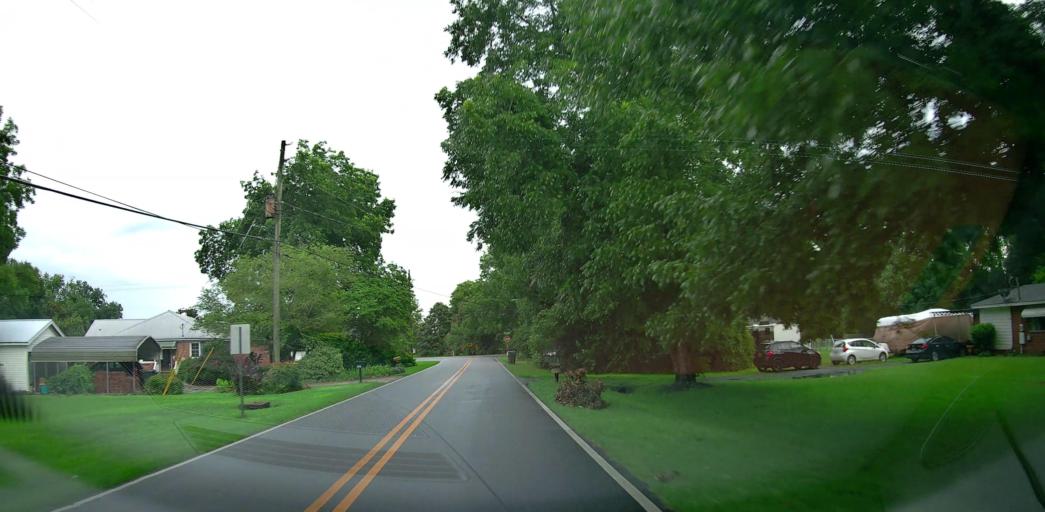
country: US
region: Georgia
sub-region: Peach County
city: Byron
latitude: 32.7320
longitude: -83.7040
